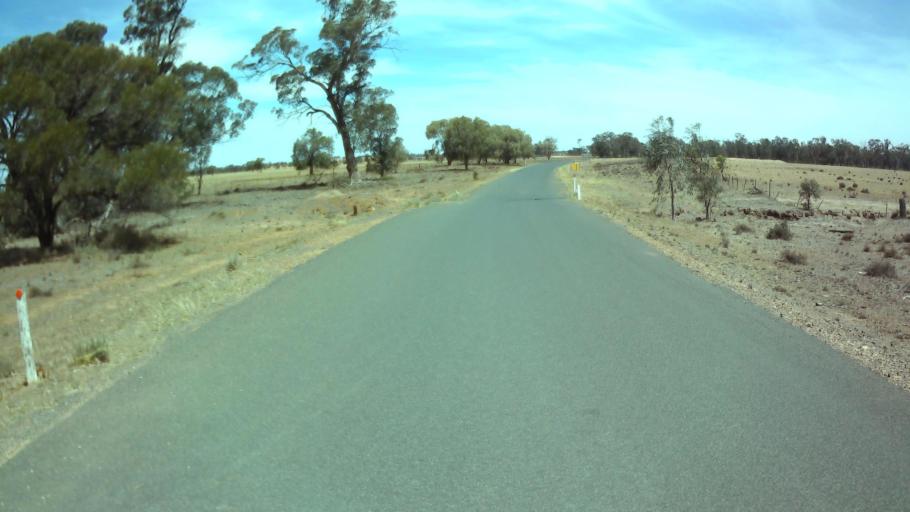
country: AU
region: New South Wales
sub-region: Weddin
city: Grenfell
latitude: -33.8588
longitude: 147.7468
